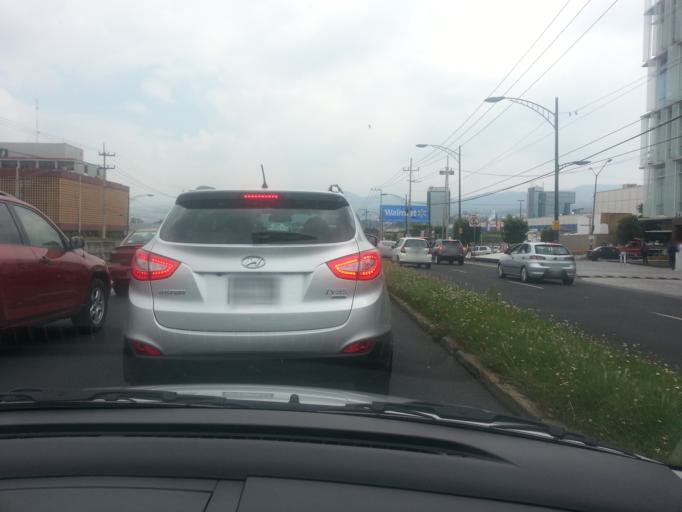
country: MX
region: Mexico City
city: Tlalpan
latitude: 19.3077
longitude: -99.1867
